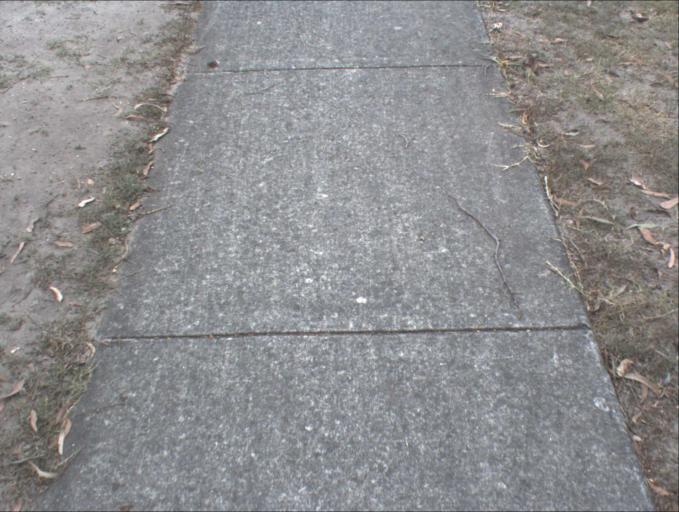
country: AU
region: Queensland
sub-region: Logan
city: Beenleigh
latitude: -27.6707
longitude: 153.1884
